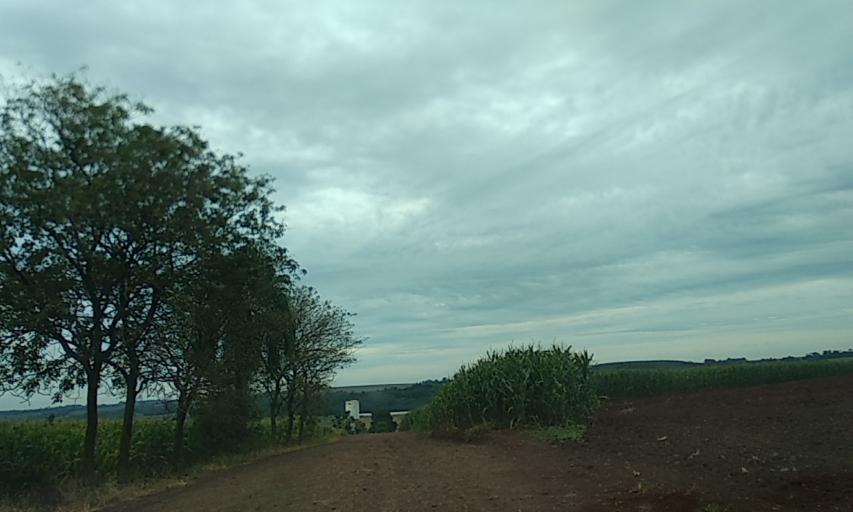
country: BR
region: Parana
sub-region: Marechal Candido Rondon
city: Marechal Candido Rondon
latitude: -24.5261
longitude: -54.0838
